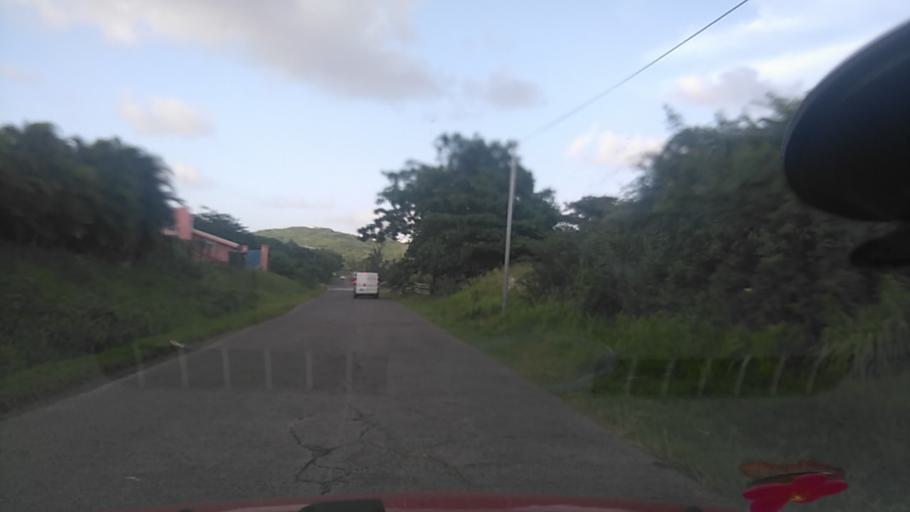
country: MQ
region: Martinique
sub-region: Martinique
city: Le Marin
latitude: 14.4677
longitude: -60.8612
